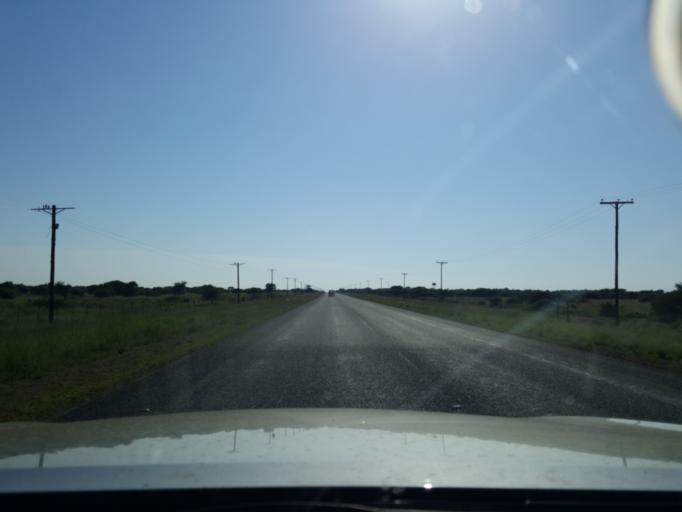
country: ZA
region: North-West
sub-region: Ngaka Modiri Molema District Municipality
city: Mahikeng
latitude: -25.8429
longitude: 25.7219
